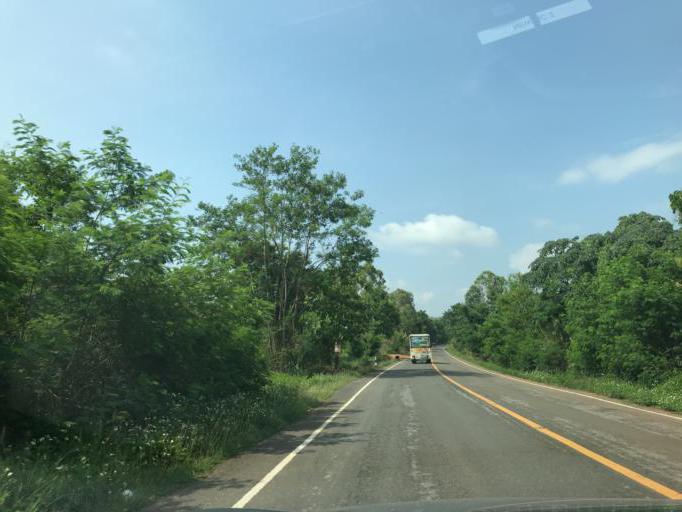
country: TH
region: Phayao
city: Chiang Kham
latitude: 19.4457
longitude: 100.3102
